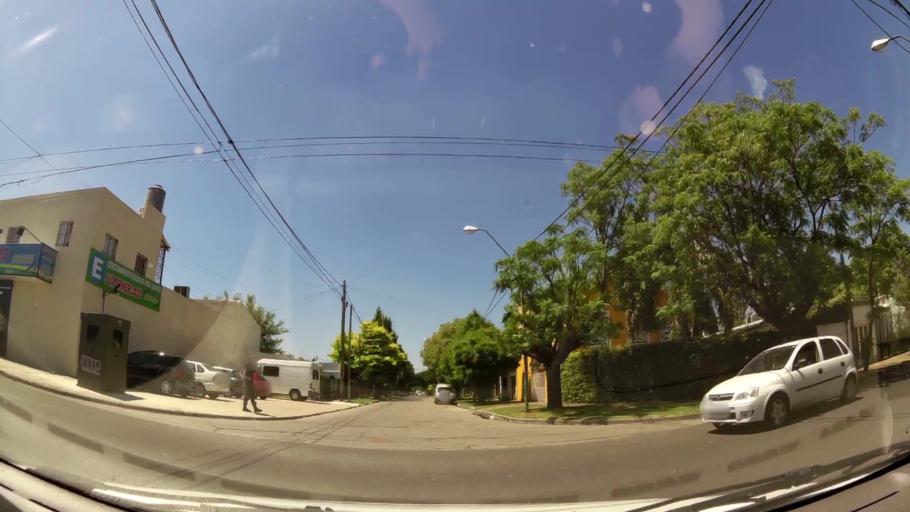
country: AR
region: Buenos Aires
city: Ituzaingo
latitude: -34.6596
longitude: -58.6779
